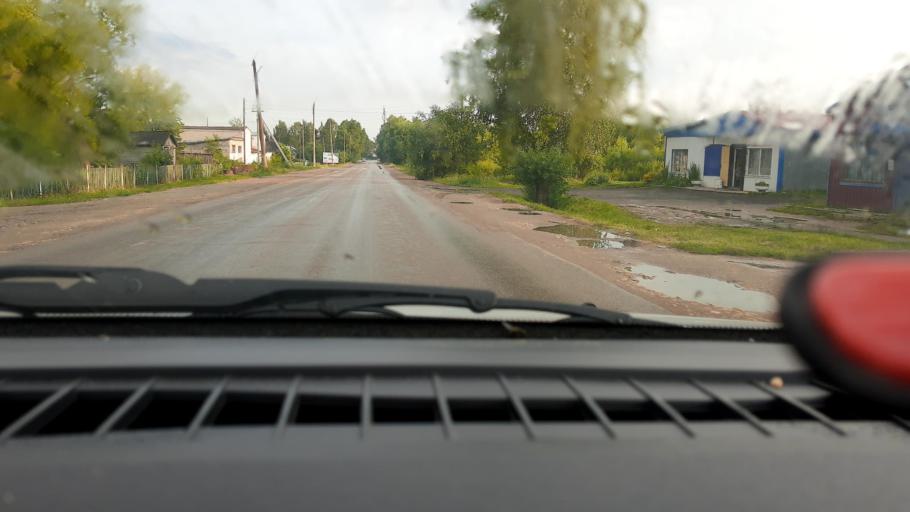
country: RU
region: Nizjnij Novgorod
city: Lukoyanov
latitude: 55.0411
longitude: 44.4971
